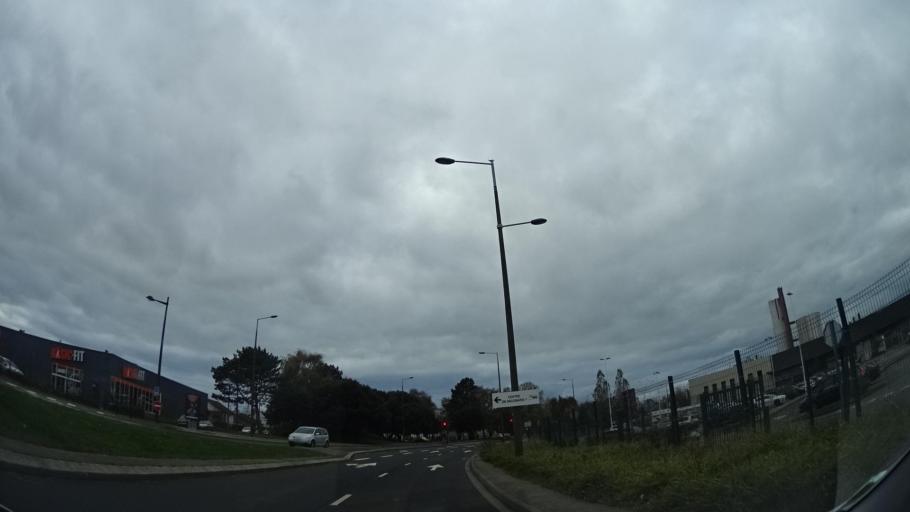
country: FR
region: Haute-Normandie
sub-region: Departement de la Seine-Maritime
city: Le Havre
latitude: 49.5204
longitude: 0.1123
